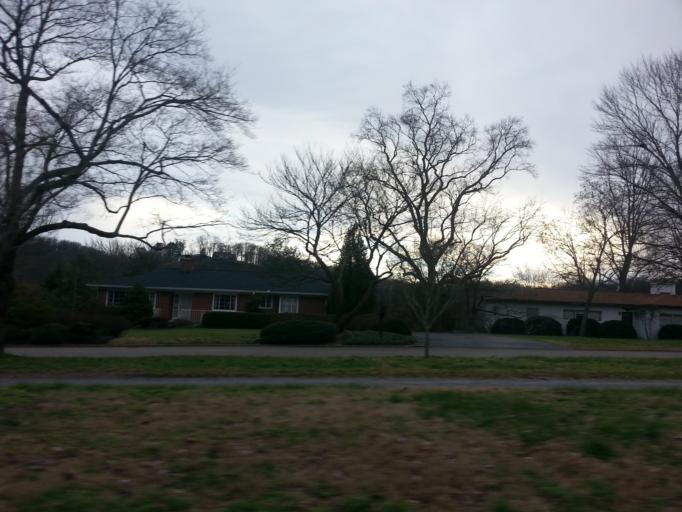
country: US
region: Tennessee
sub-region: Knox County
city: Knoxville
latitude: 35.9289
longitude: -83.9706
